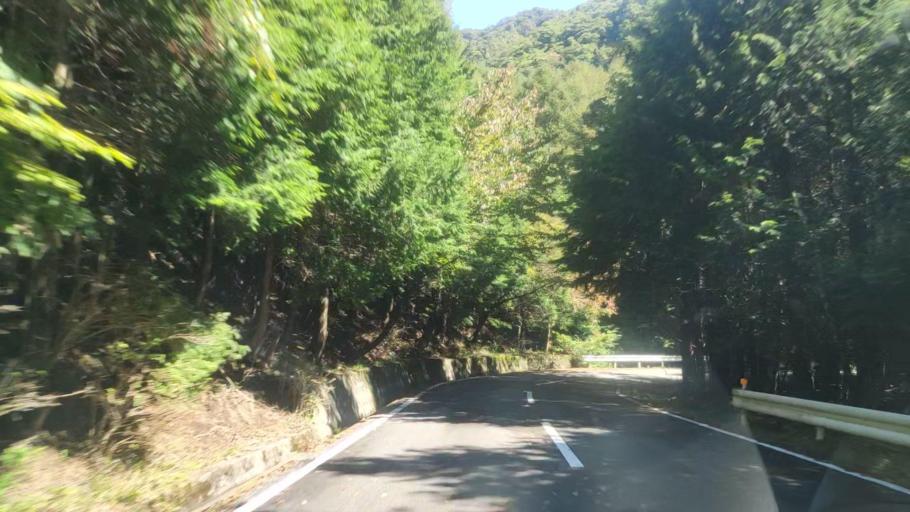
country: JP
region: Yamanashi
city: Fujikawaguchiko
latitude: 35.5678
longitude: 138.7838
